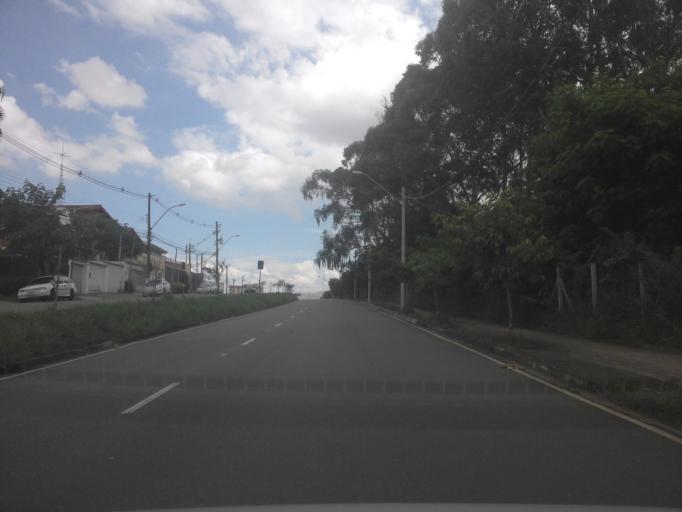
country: BR
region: Sao Paulo
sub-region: Campinas
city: Campinas
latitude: -22.8707
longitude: -47.0323
